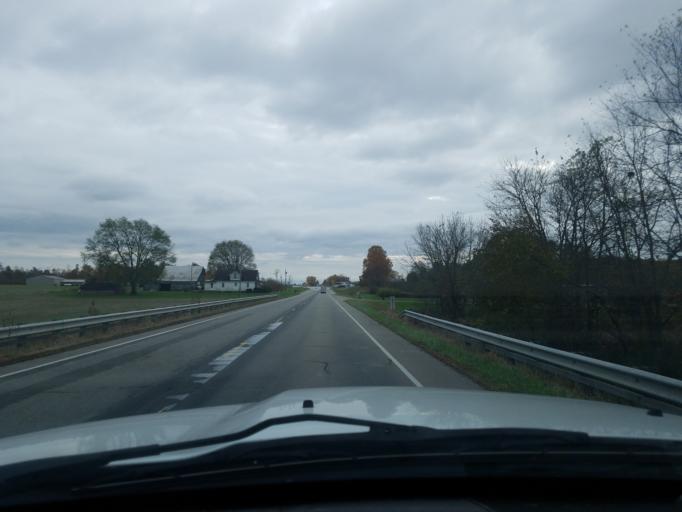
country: US
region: Indiana
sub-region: Bartholomew County
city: Hope
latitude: 39.2308
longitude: -85.7719
